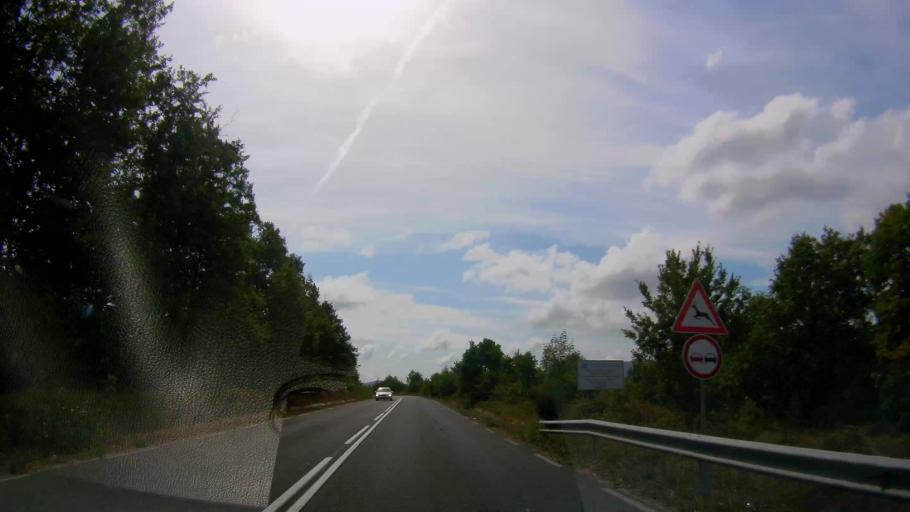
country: BG
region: Burgas
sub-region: Obshtina Sozopol
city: Sozopol
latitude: 42.3715
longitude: 27.6833
